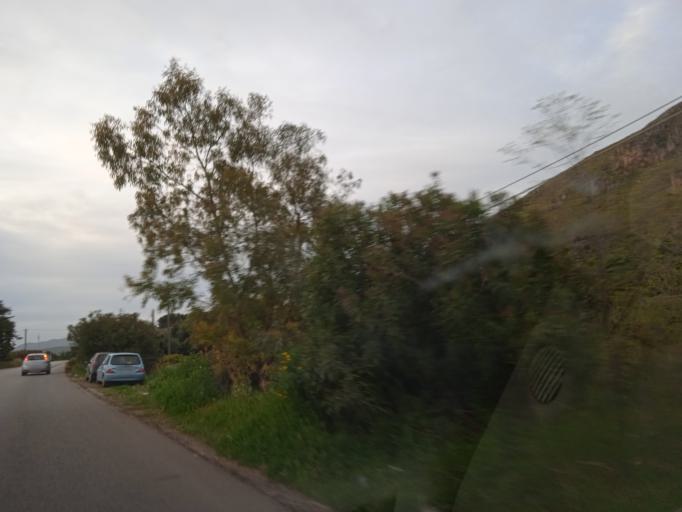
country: IT
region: Sicily
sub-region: Palermo
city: Portella di Mare
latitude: 38.0607
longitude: 13.4608
